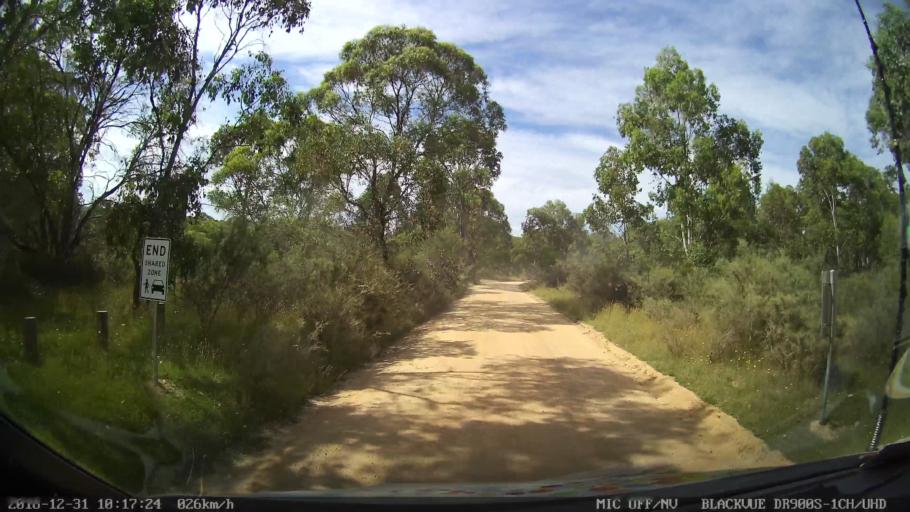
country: AU
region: New South Wales
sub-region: Snowy River
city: Jindabyne
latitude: -36.5397
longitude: 148.1346
